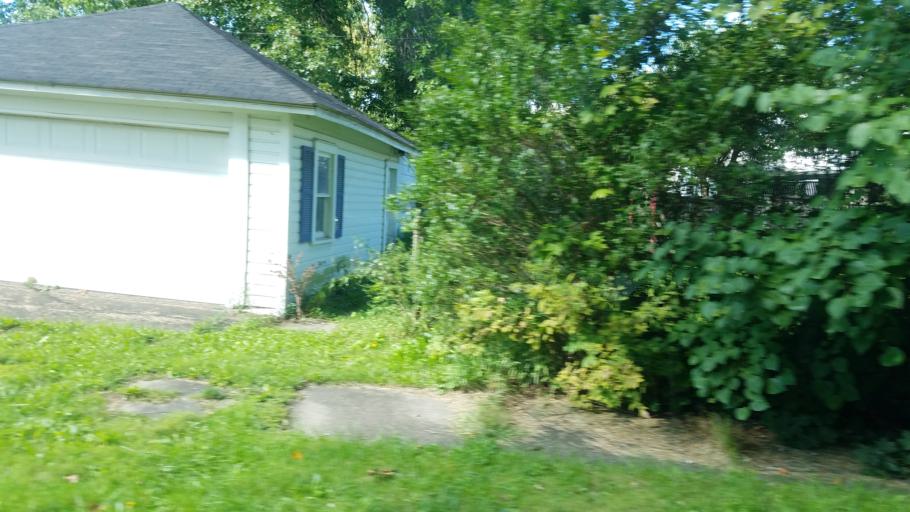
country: US
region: Ohio
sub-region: Trumbull County
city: Niles
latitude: 41.1842
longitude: -80.7489
